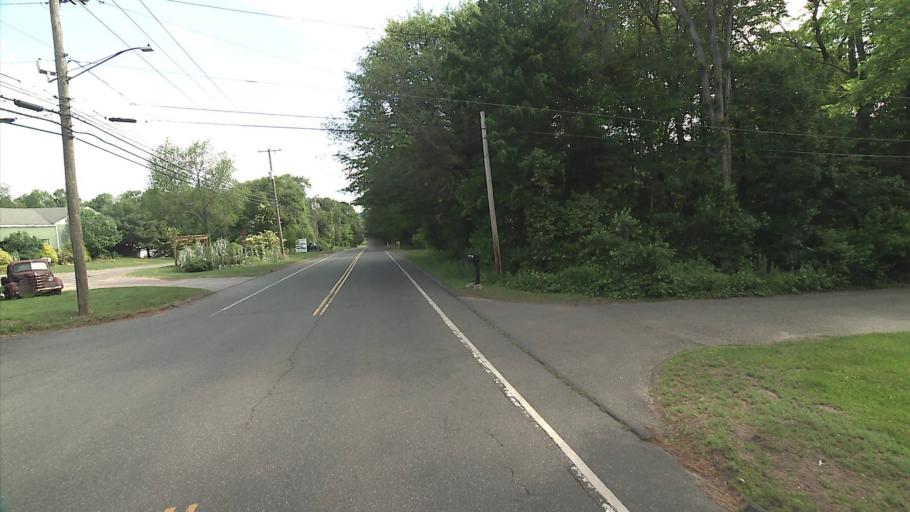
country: US
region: Connecticut
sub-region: New Haven County
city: Prospect
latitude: 41.4437
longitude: -72.9898
